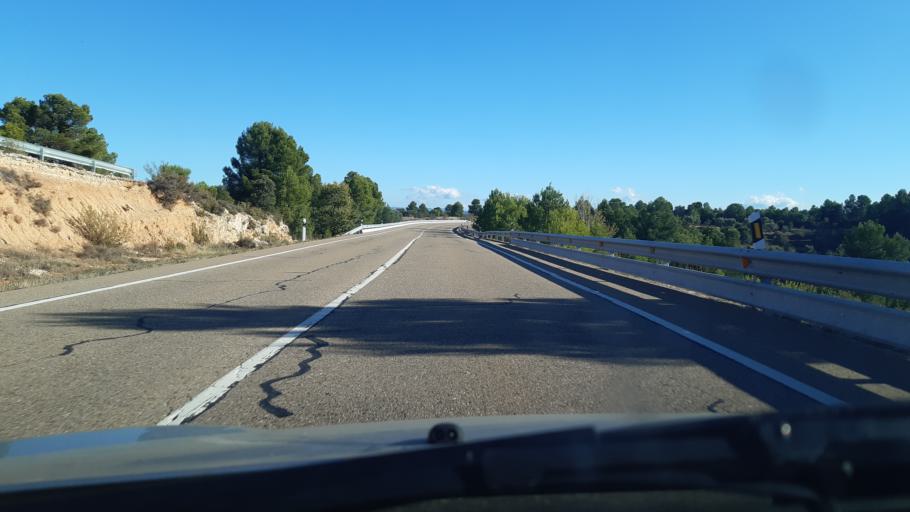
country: ES
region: Aragon
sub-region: Provincia de Teruel
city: Valjunquera
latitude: 40.9525
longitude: -0.0133
